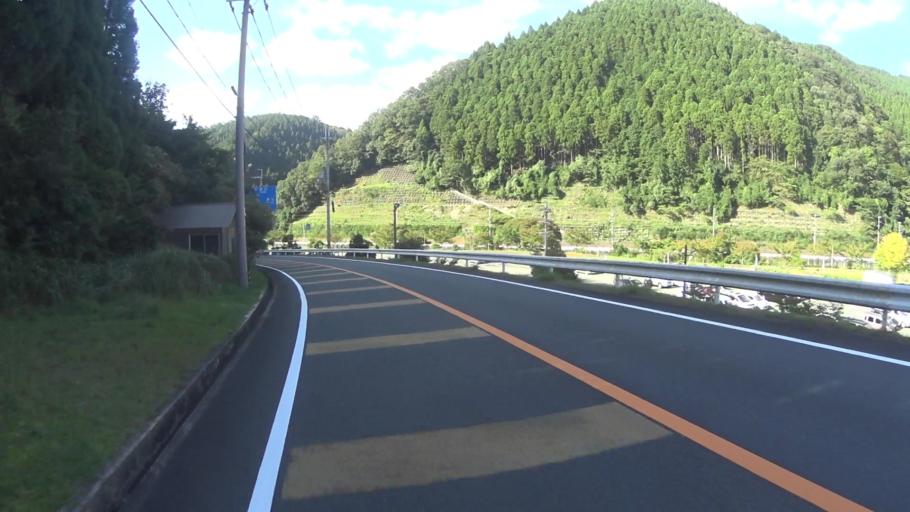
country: JP
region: Kyoto
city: Kameoka
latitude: 35.1525
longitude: 135.5154
